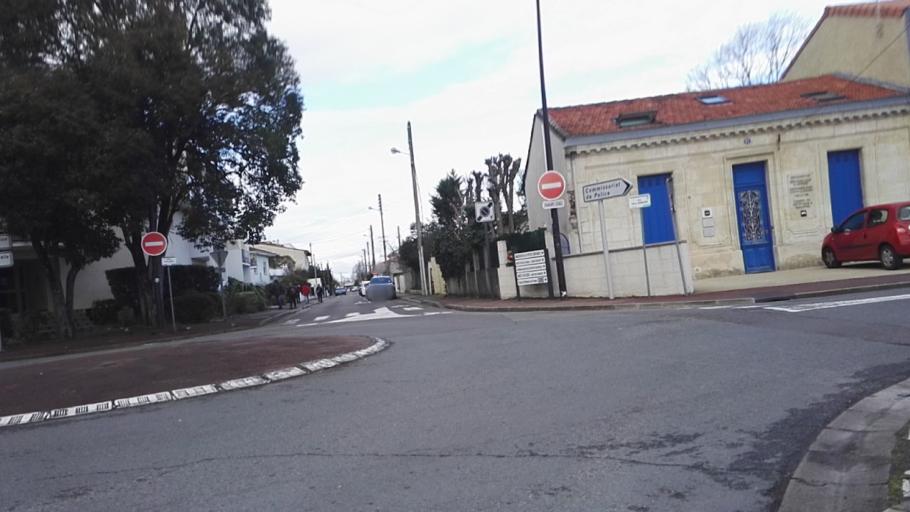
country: FR
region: Aquitaine
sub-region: Departement de la Gironde
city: Talence
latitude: 44.8139
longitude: -0.5918
